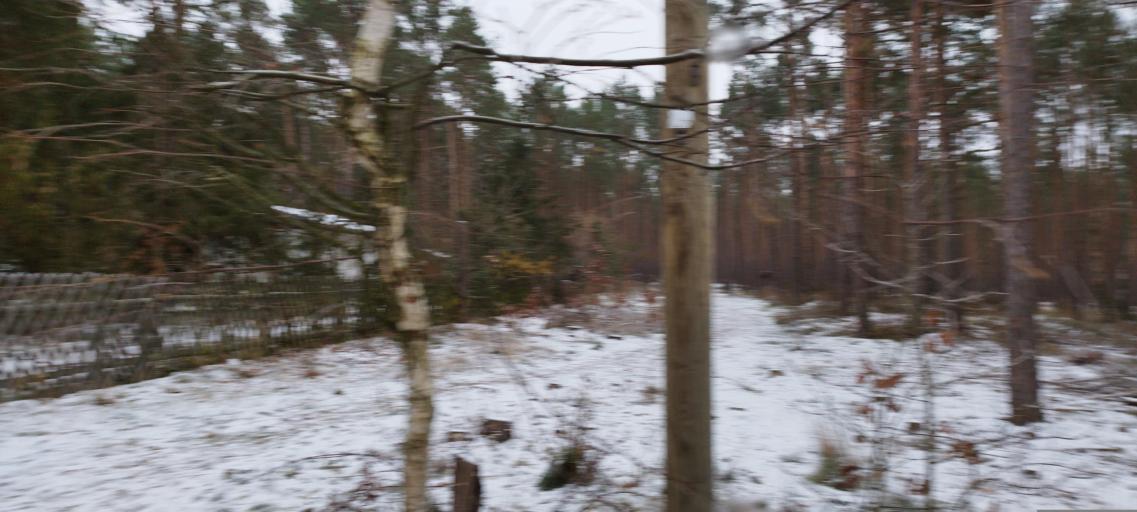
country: DE
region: Brandenburg
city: Gross Koris
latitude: 52.1584
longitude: 13.6964
